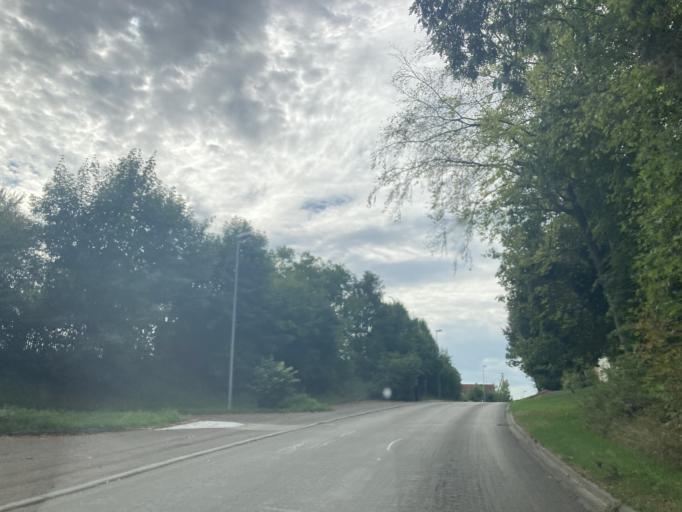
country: DE
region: Bavaria
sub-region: Swabia
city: Mottingen
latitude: 48.8120
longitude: 10.6037
